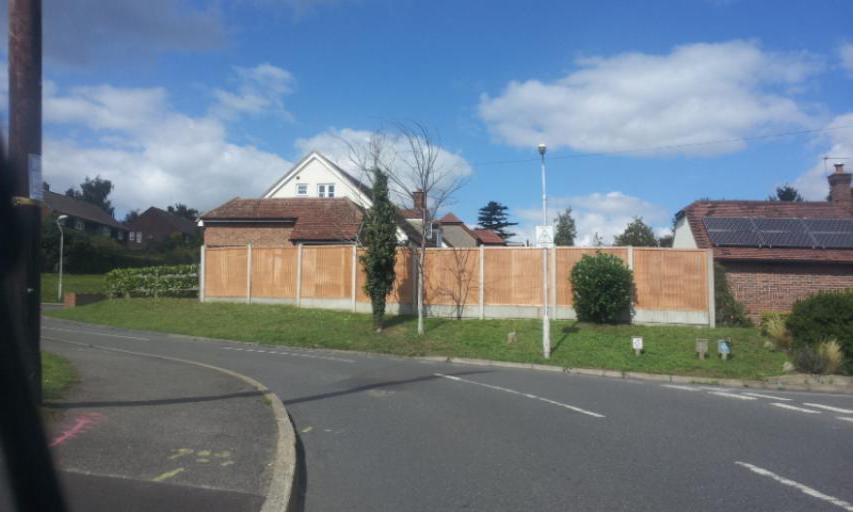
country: GB
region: England
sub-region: Kent
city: Larkfield
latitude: 51.2967
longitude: 0.4482
